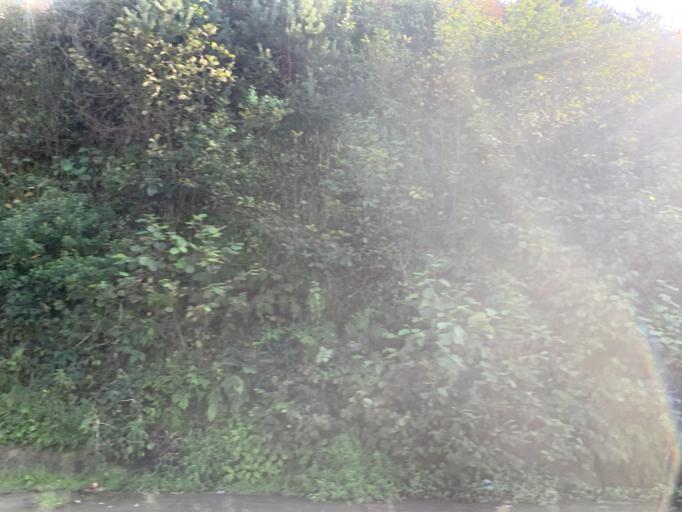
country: TR
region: Trabzon
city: Of
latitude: 40.9265
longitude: 40.2269
